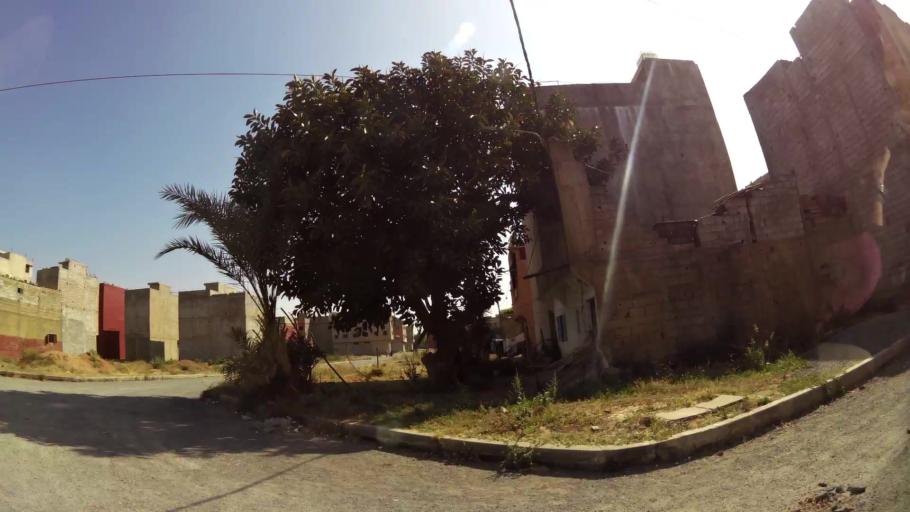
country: MA
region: Rabat-Sale-Zemmour-Zaer
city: Sale
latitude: 34.0637
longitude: -6.7665
